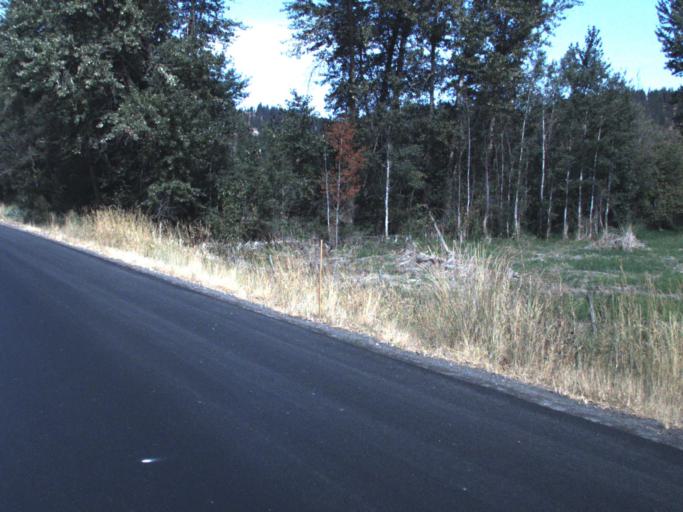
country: US
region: Washington
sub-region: Stevens County
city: Colville
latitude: 48.4657
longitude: -117.8863
